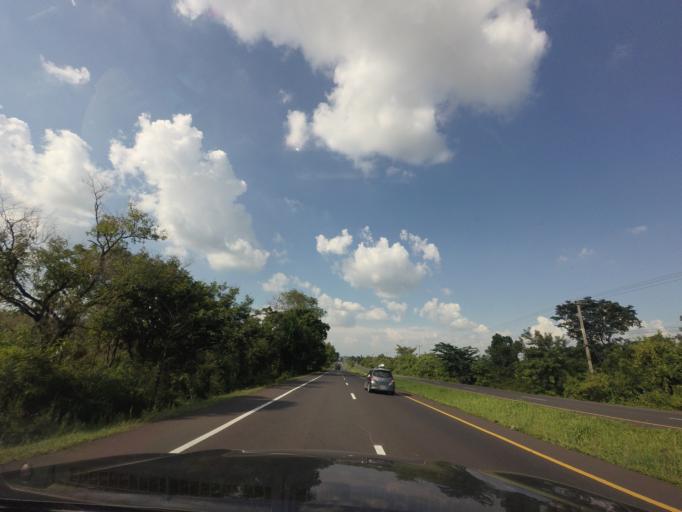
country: TH
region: Nakhon Ratchasima
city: Bua Lai
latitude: 15.6988
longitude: 102.5833
